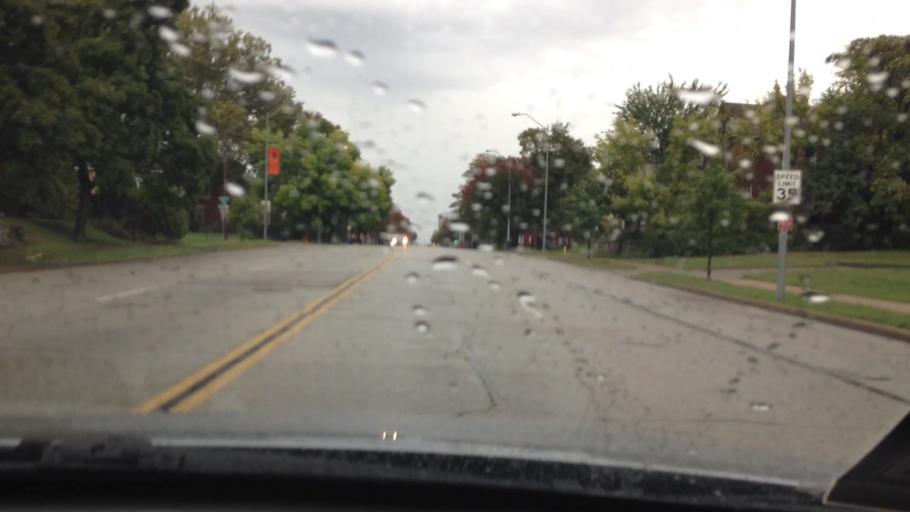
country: US
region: Missouri
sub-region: Jackson County
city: Kansas City
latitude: 39.0606
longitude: -94.5672
